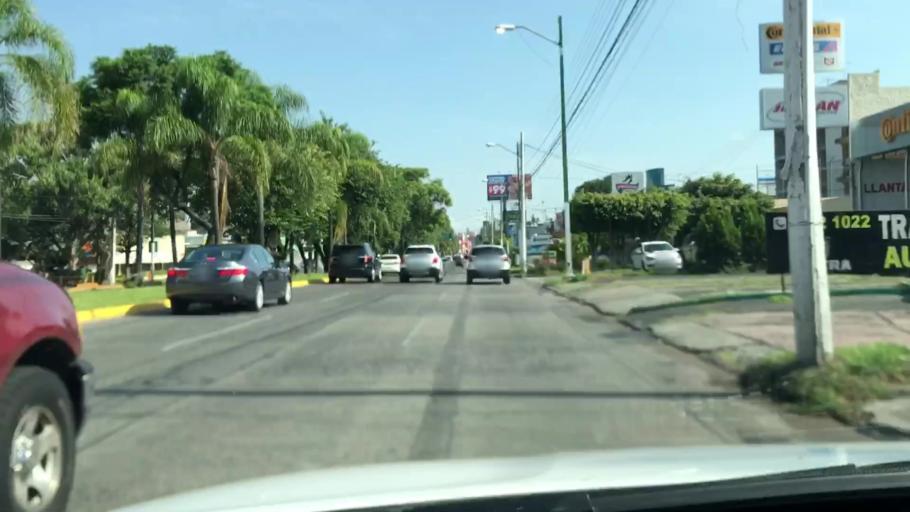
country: MX
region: Jalisco
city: Guadalajara
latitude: 20.6655
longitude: -103.4240
